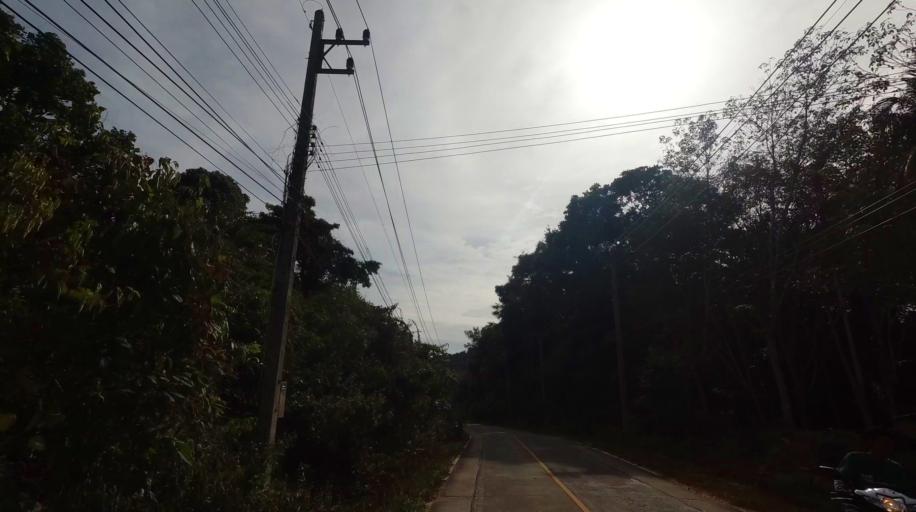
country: TH
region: Trat
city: Ko Kut
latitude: 11.6127
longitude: 102.5425
